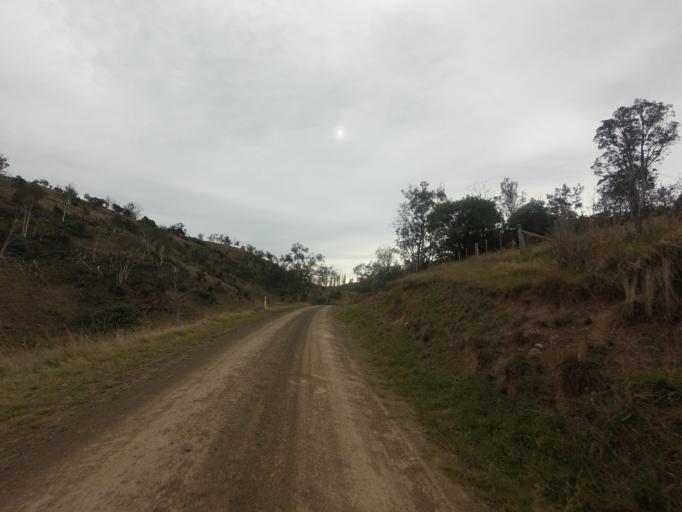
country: AU
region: Tasmania
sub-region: Derwent Valley
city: New Norfolk
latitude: -42.3605
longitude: 146.8409
